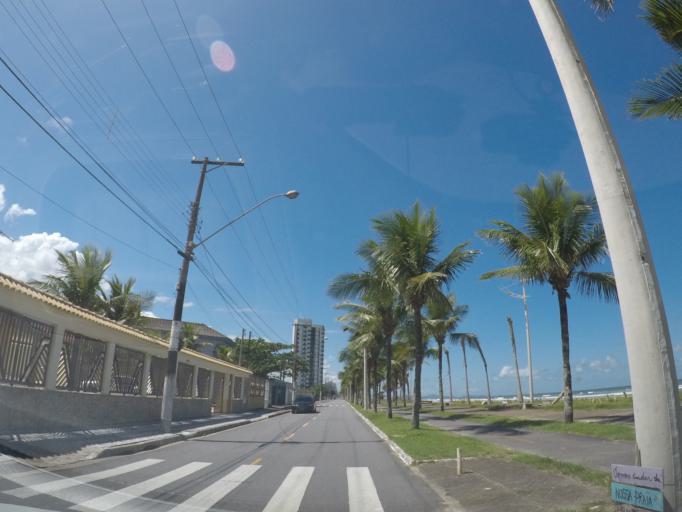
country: BR
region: Sao Paulo
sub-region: Mongagua
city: Mongagua
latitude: -24.0793
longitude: -46.5859
